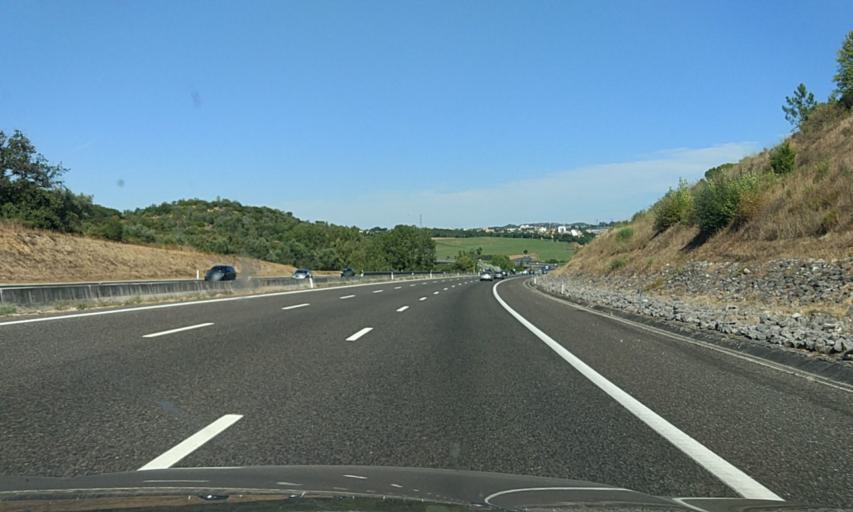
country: PT
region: Santarem
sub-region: Santarem
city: Santarem
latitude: 39.2361
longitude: -8.7561
